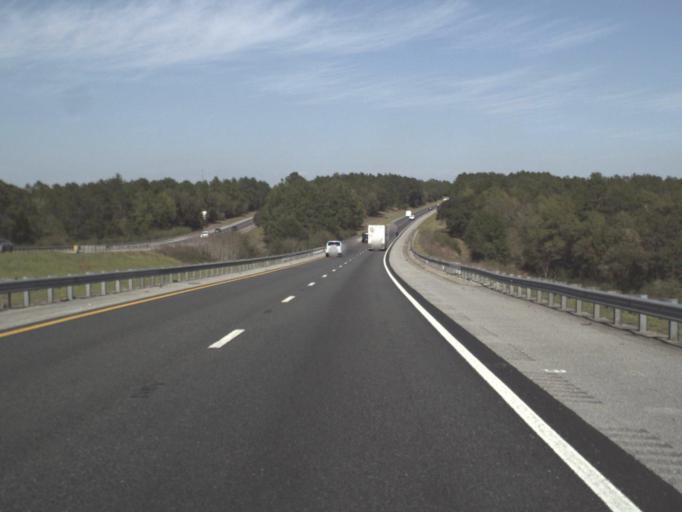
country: US
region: Florida
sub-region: Okaloosa County
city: Crestview
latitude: 30.7044
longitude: -86.7359
